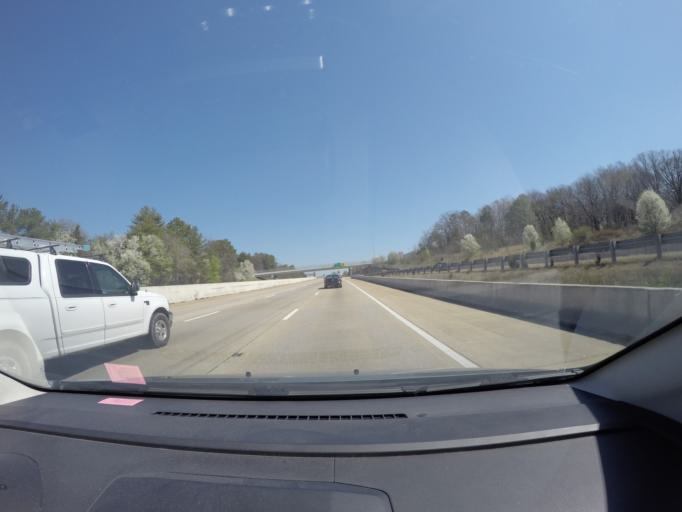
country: US
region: Tennessee
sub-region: Hamilton County
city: East Brainerd
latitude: 35.0311
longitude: -85.1682
